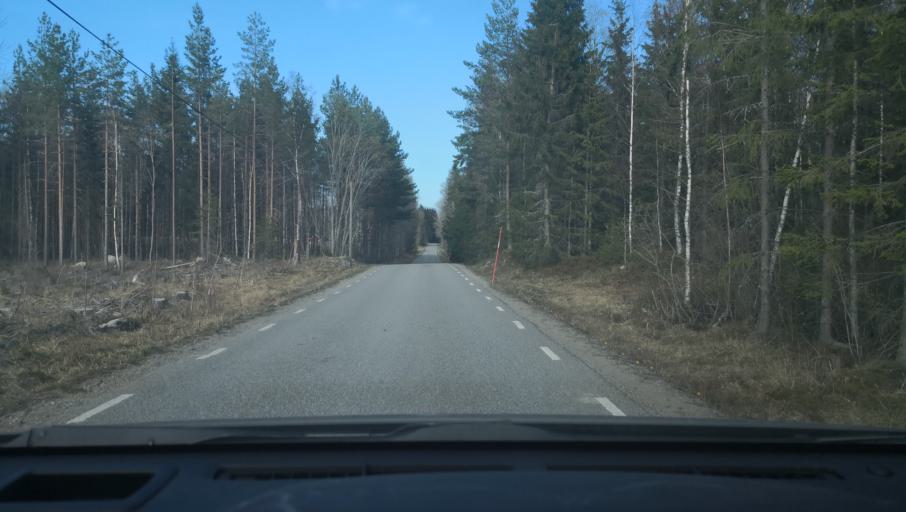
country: SE
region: Uppsala
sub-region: Heby Kommun
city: Heby
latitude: 59.9183
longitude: 16.8404
